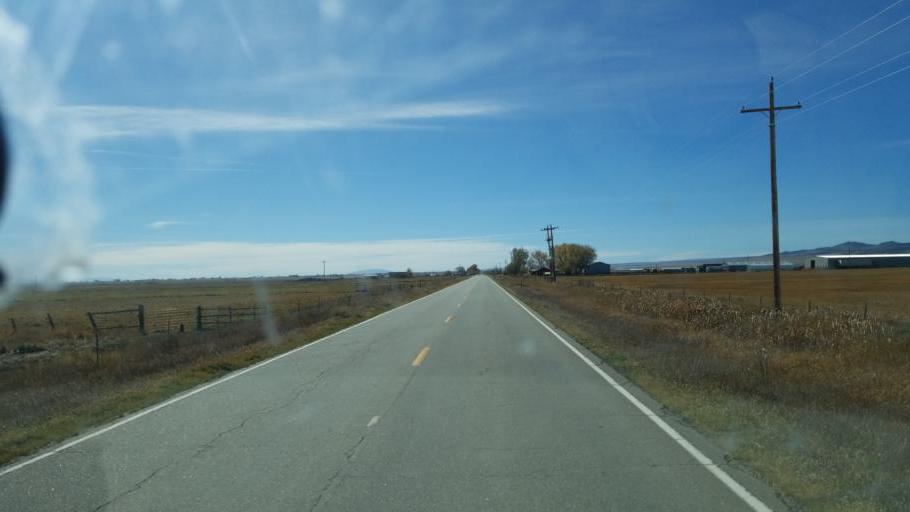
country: US
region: Colorado
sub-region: Rio Grande County
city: Monte Vista
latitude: 37.5050
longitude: -106.1492
